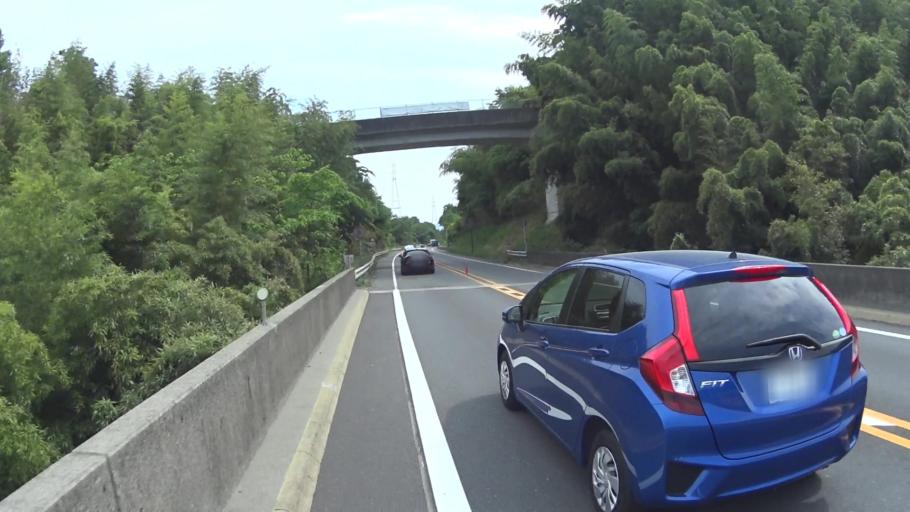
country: JP
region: Shiga Prefecture
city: Kitahama
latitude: 35.1158
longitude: 135.8983
